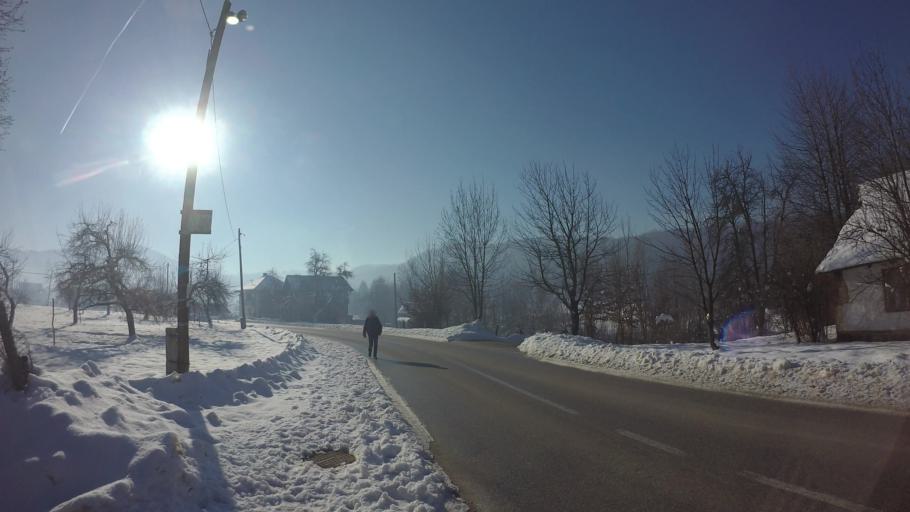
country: BA
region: Federation of Bosnia and Herzegovina
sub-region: Kanton Sarajevo
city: Sarajevo
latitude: 43.8166
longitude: 18.3835
